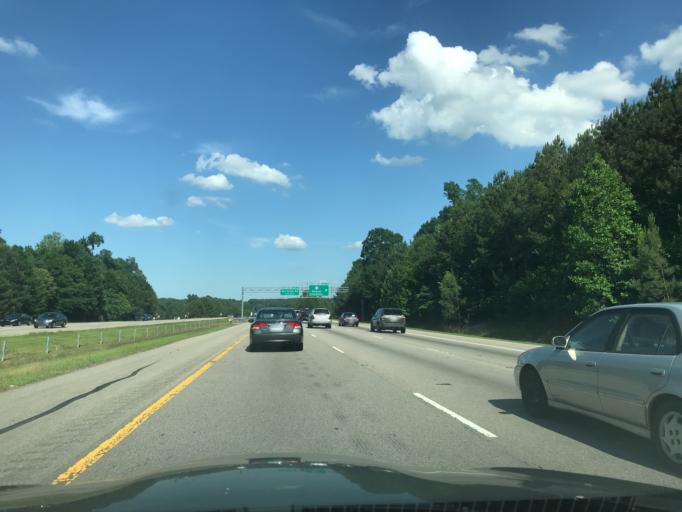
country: US
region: North Carolina
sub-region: Wake County
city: West Raleigh
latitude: 35.9154
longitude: -78.6886
